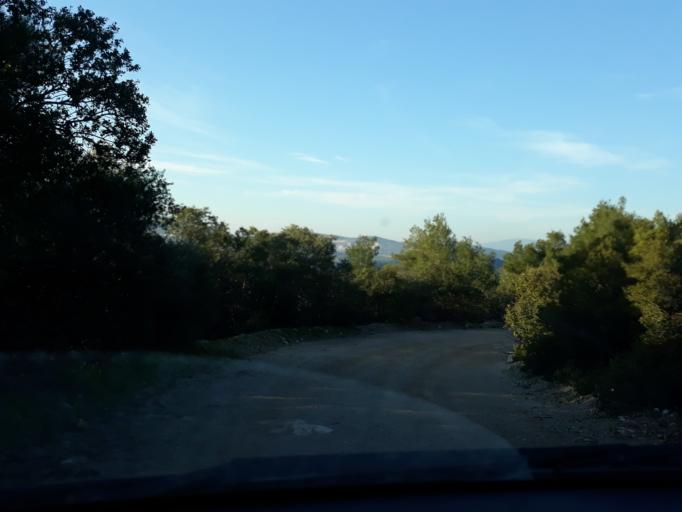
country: GR
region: Central Greece
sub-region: Nomos Voiotias
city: Asopia
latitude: 38.2725
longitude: 23.5328
